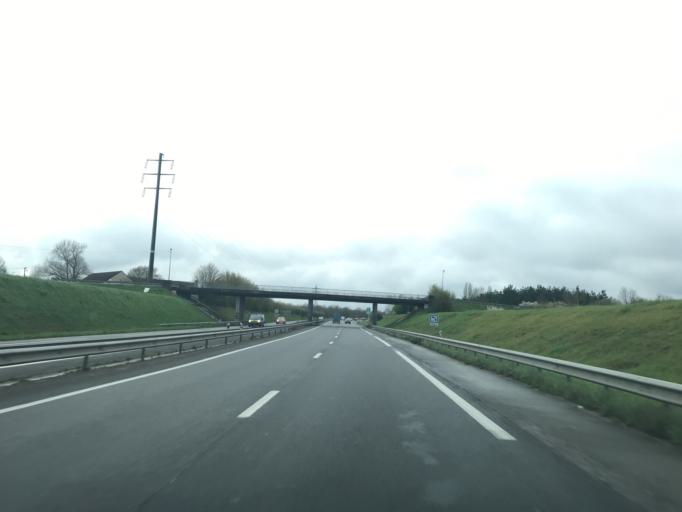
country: FR
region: Centre
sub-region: Departement du Loiret
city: Boigny-sur-Bionne
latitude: 47.9197
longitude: 2.0025
